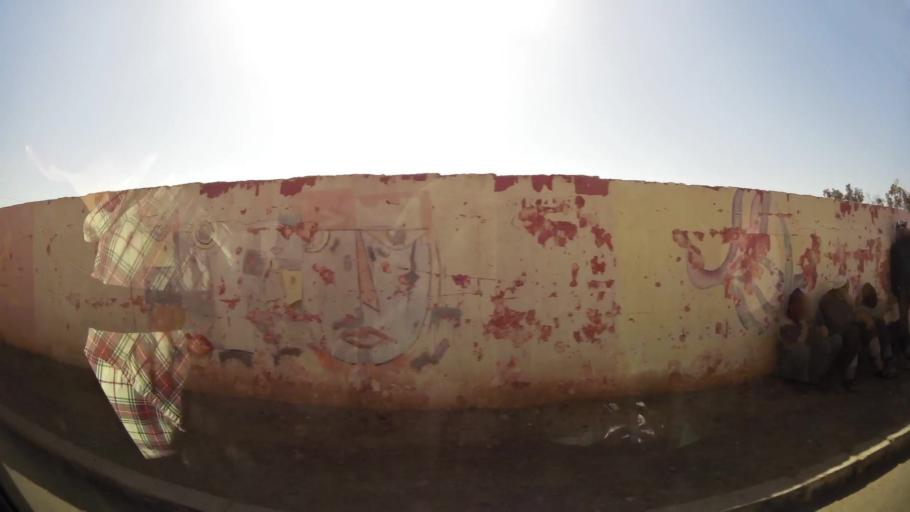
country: MA
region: Souss-Massa-Draa
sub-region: Inezgane-Ait Mellou
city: Inezgane
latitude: 30.3331
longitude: -9.5180
